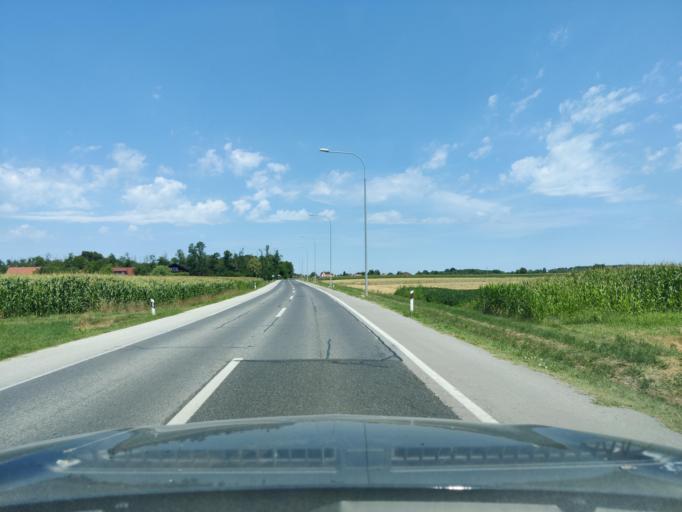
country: HR
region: Medimurska
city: Senkovec
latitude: 46.4158
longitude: 16.4245
